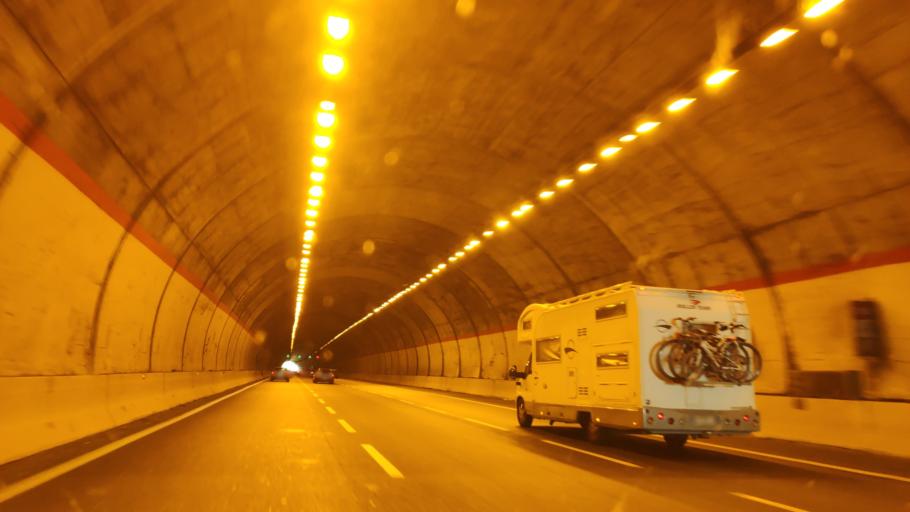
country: IT
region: Campania
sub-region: Provincia di Salerno
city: Piegolelle-San Bartolomeo
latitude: 40.6989
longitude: 14.8182
